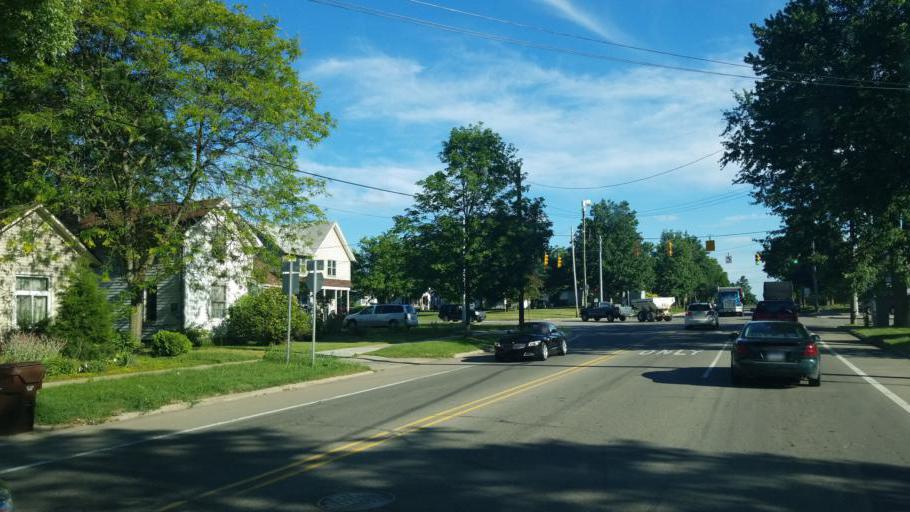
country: US
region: Michigan
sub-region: Eaton County
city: Charlotte
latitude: 42.5542
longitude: -84.8359
